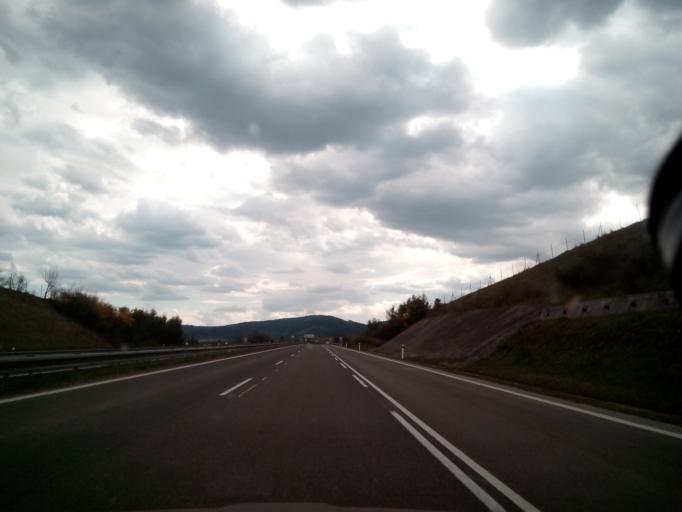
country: SK
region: Kosicky
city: Krompachy
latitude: 49.0036
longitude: 20.9329
